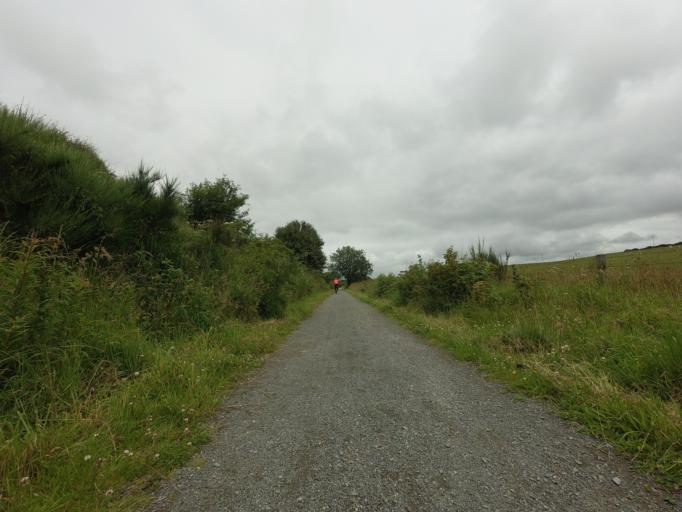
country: GB
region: Scotland
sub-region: Aberdeenshire
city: Mintlaw
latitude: 57.5147
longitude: -2.1365
